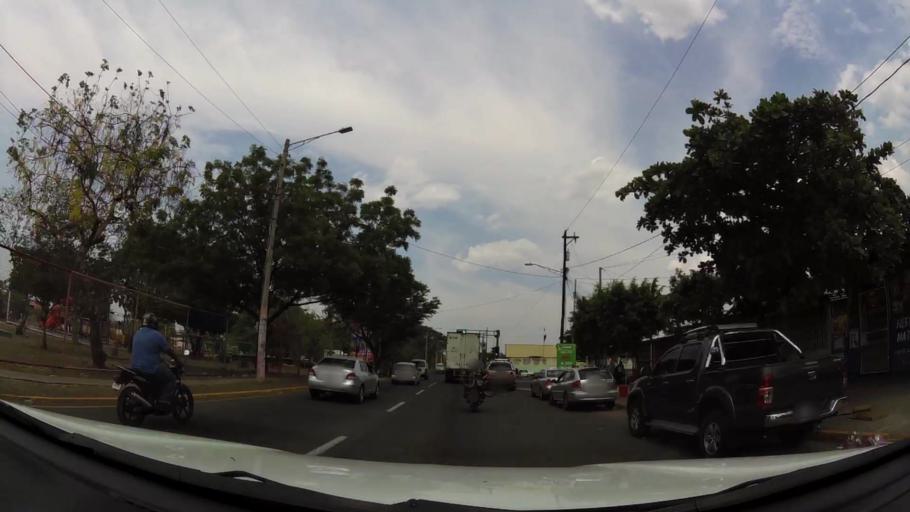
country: NI
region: Managua
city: Managua
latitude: 12.1549
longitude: -86.2830
